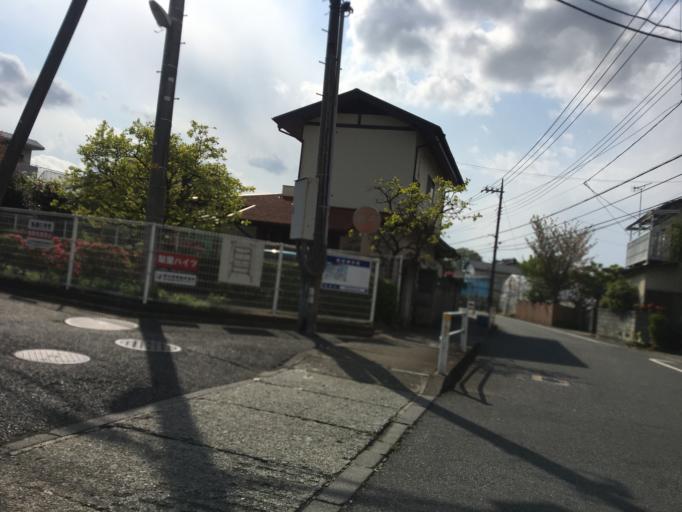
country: JP
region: Tokyo
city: Chofugaoka
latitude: 35.6446
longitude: 139.5073
